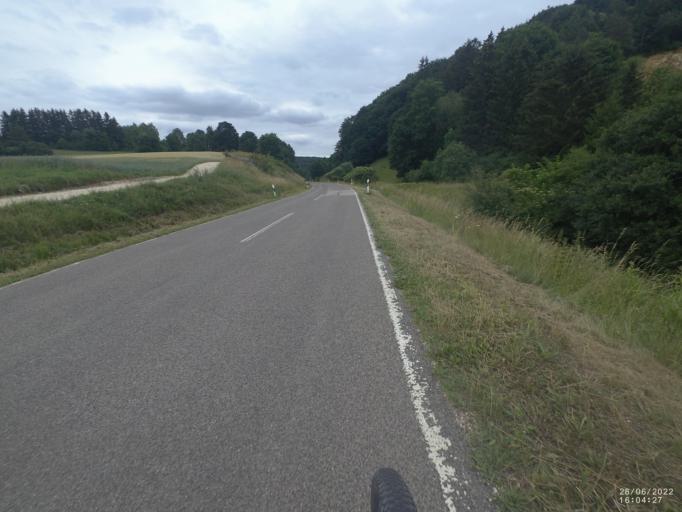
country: DE
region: Baden-Wuerttemberg
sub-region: Regierungsbezirk Stuttgart
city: Gerstetten
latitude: 48.6454
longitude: 10.0072
